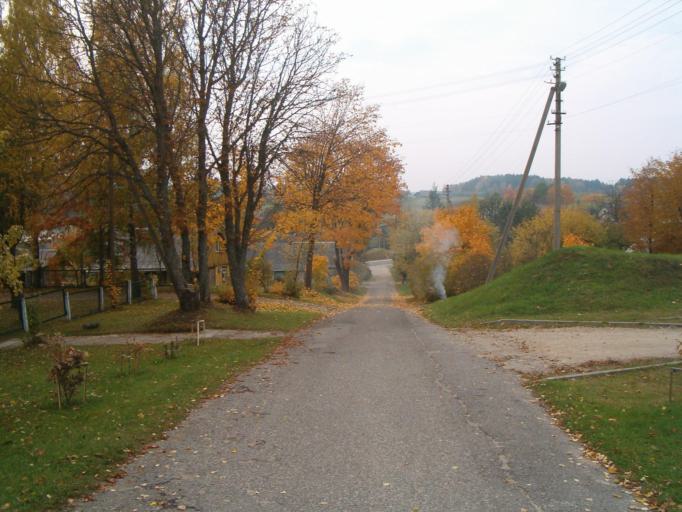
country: LT
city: Zarasai
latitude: 55.6585
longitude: 26.0577
